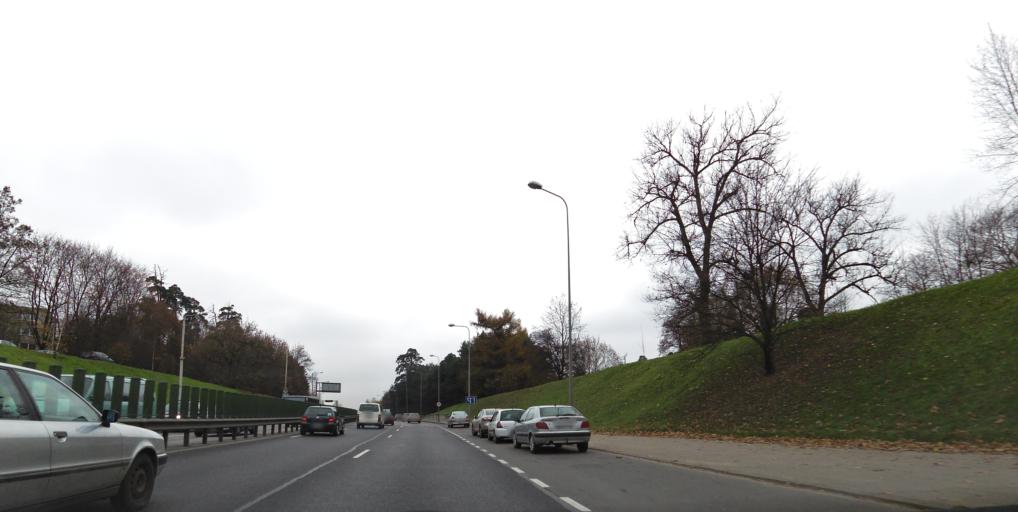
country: LT
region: Vilnius County
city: Vilkpede
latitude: 54.6822
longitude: 25.2487
